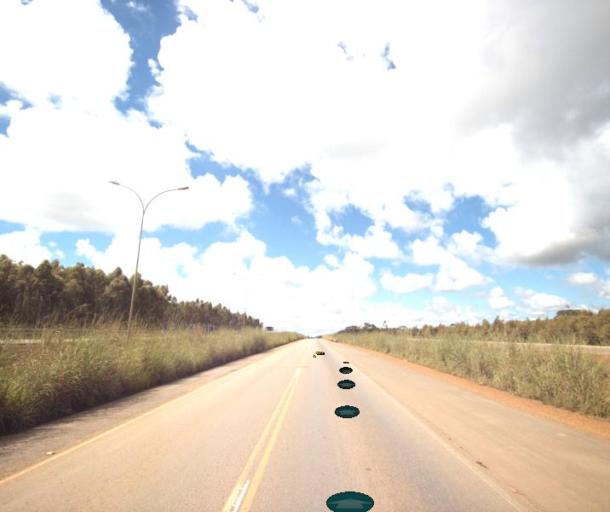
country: BR
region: Goias
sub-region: Anapolis
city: Anapolis
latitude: -16.2344
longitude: -49.0070
